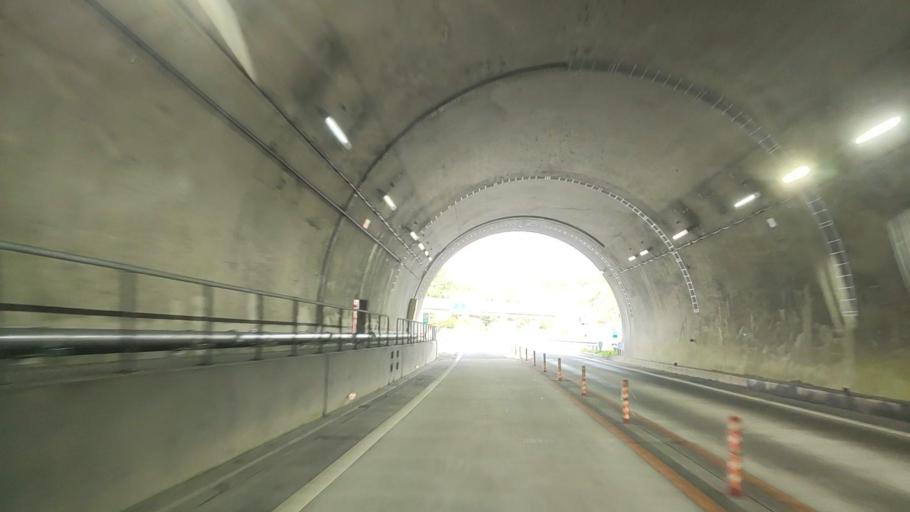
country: JP
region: Ehime
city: Hojo
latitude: 34.0874
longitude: 132.9784
